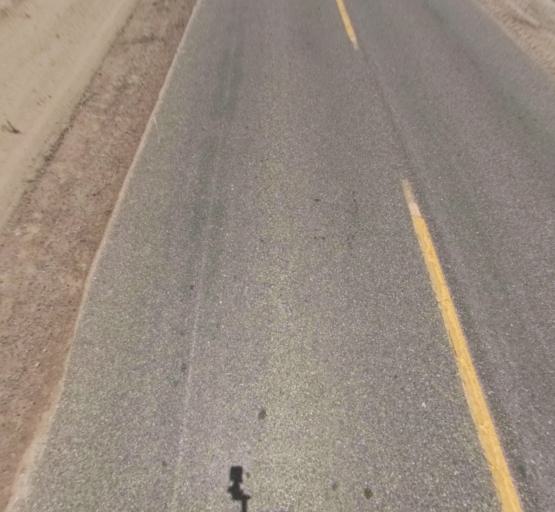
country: US
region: California
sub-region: Madera County
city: Parkwood
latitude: 36.8992
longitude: -120.0924
